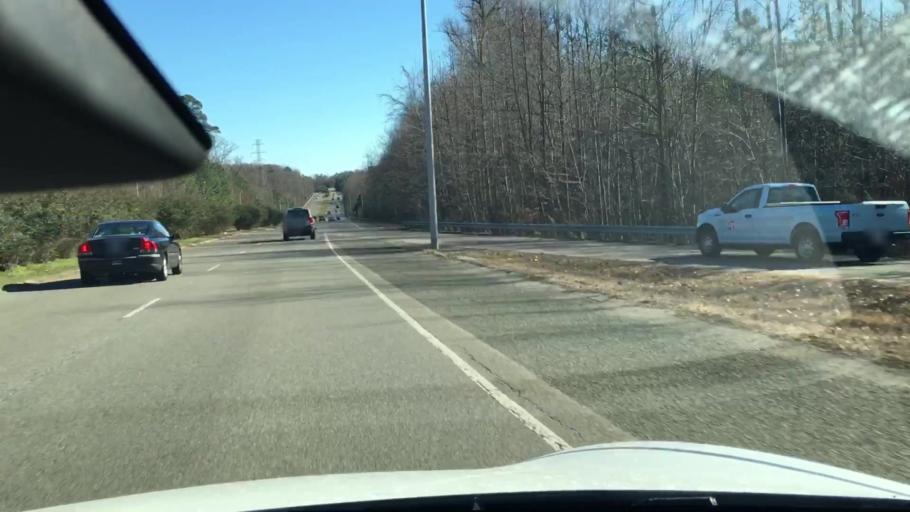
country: US
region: Virginia
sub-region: Chesterfield County
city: Bon Air
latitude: 37.5497
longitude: -77.5660
